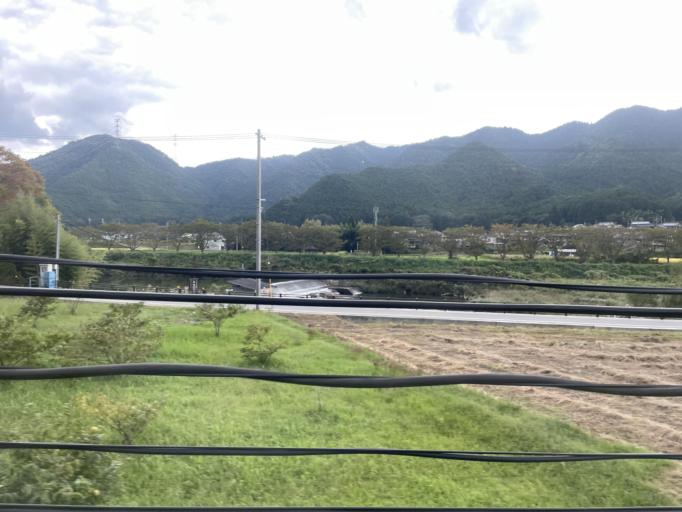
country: JP
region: Hyogo
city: Nishiwaki
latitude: 35.0843
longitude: 135.0628
